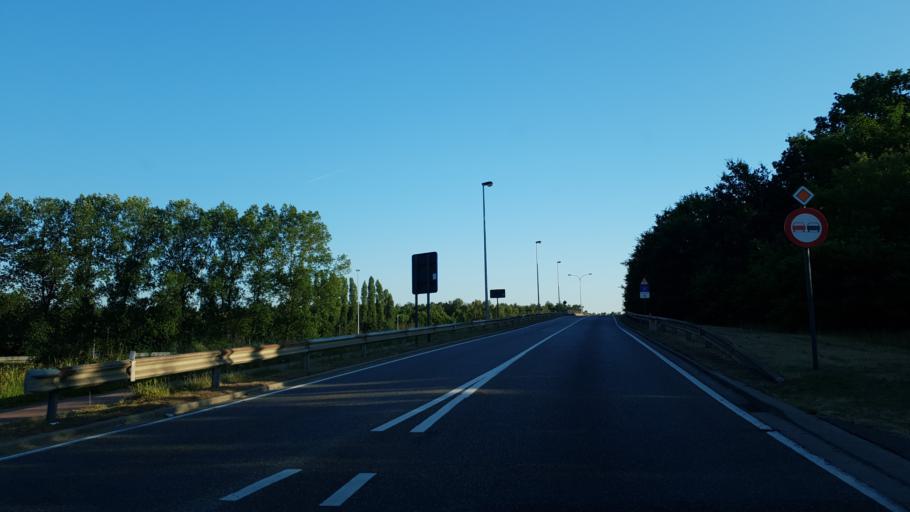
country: BE
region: Flanders
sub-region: Provincie Antwerpen
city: Beerse
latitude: 51.2845
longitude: 4.8567
